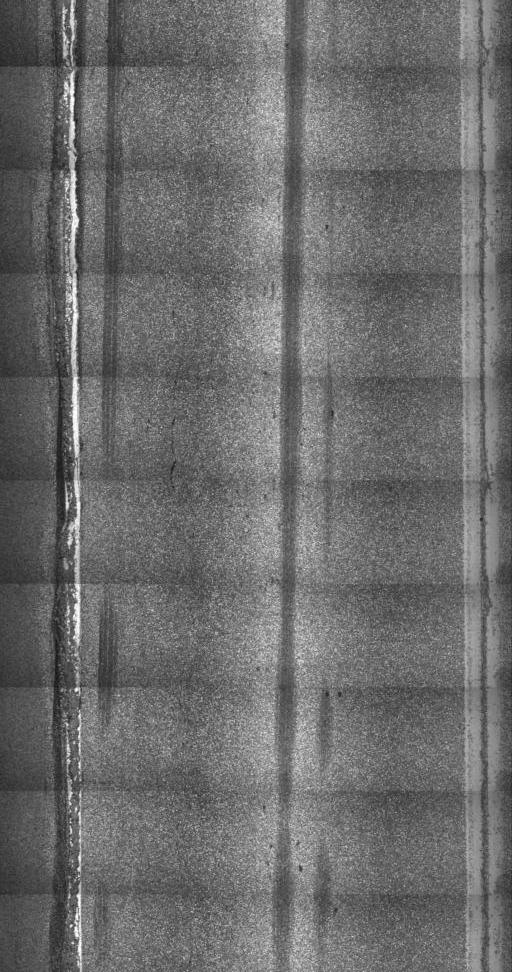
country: US
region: Vermont
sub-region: Washington County
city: Barre
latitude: 44.2584
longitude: -72.4857
